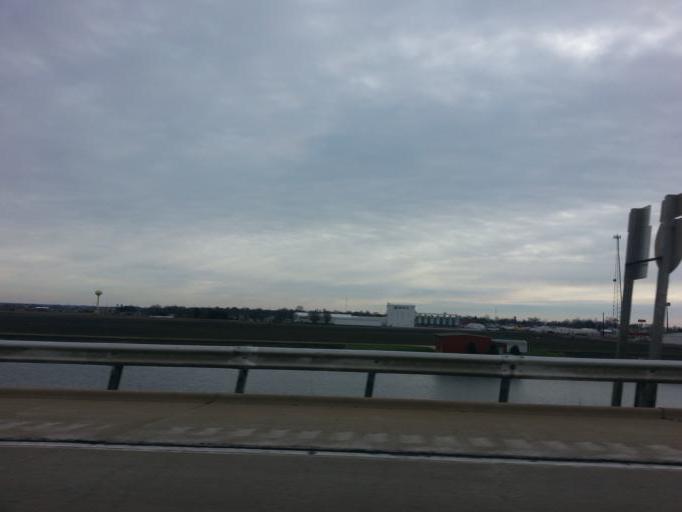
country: US
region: Illinois
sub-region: Woodford County
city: El Paso
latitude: 40.7390
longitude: -89.0343
